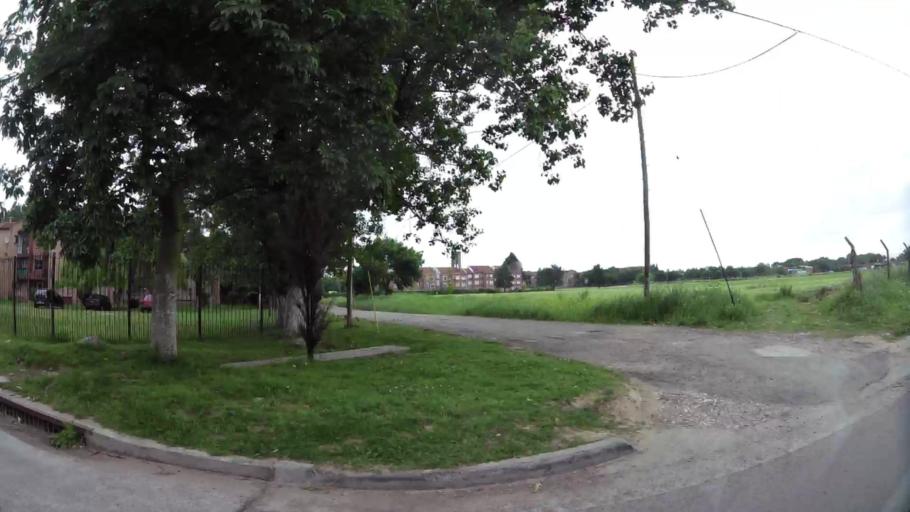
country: AR
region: Buenos Aires
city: San Justo
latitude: -34.7139
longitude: -58.5256
